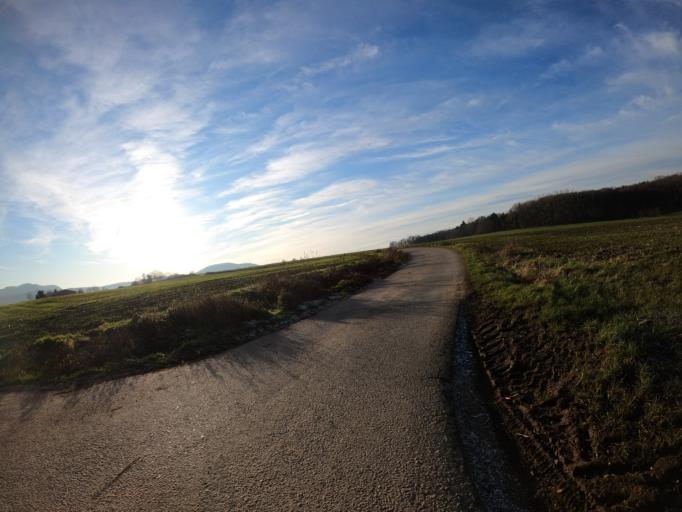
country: DE
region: Baden-Wuerttemberg
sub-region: Regierungsbezirk Stuttgart
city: Boll
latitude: 48.6558
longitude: 9.6091
